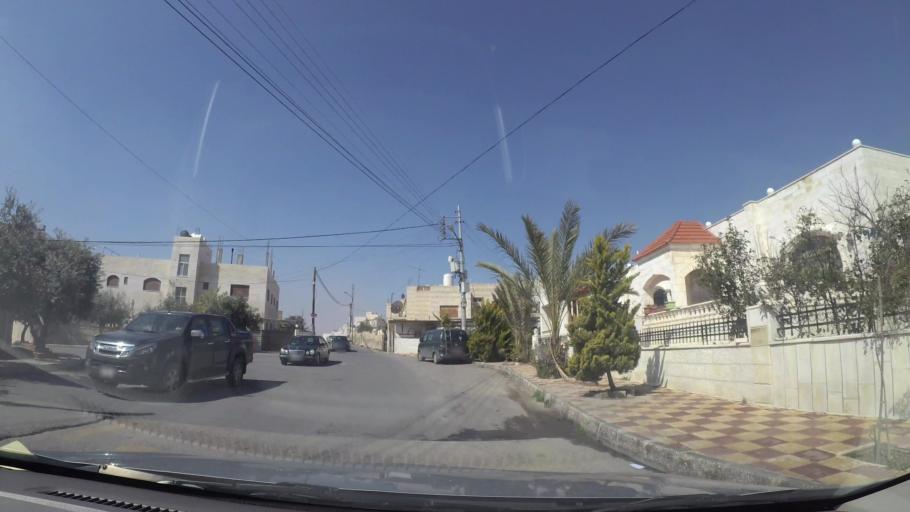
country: JO
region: Amman
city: Al Bunayyat ash Shamaliyah
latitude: 31.8985
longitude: 35.8839
